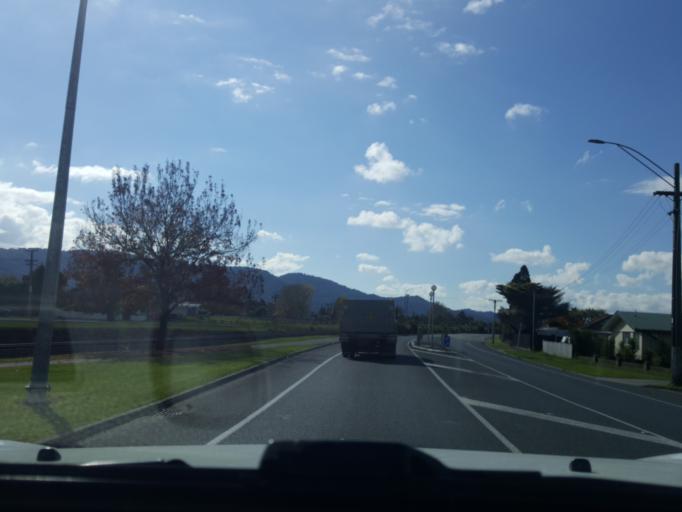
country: NZ
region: Waikato
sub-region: Waikato District
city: Ngaruawahia
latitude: -37.6615
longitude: 175.1496
